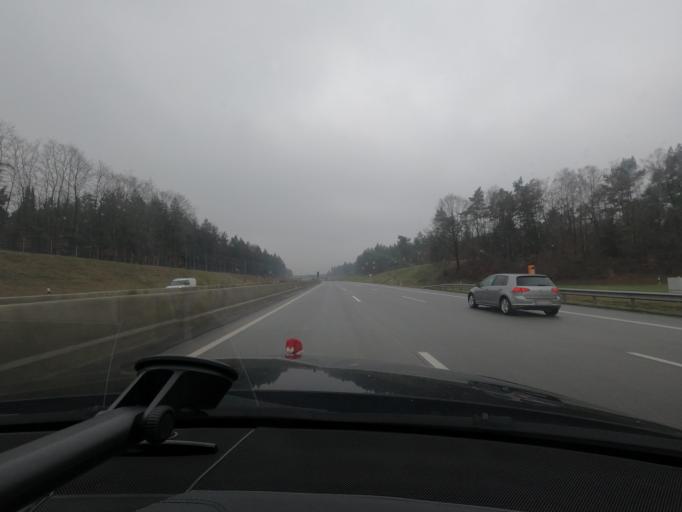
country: DE
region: Schleswig-Holstein
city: Bimohlen
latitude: 53.9025
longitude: 9.9372
